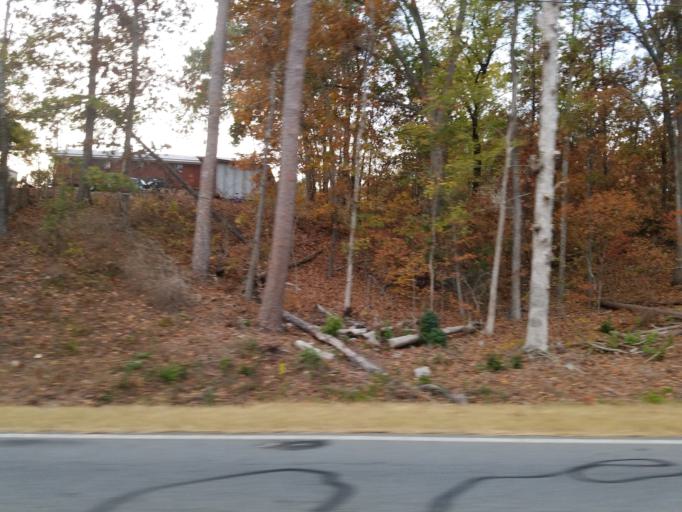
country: US
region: Georgia
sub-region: Gordon County
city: Calhoun
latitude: 34.5906
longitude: -84.9345
